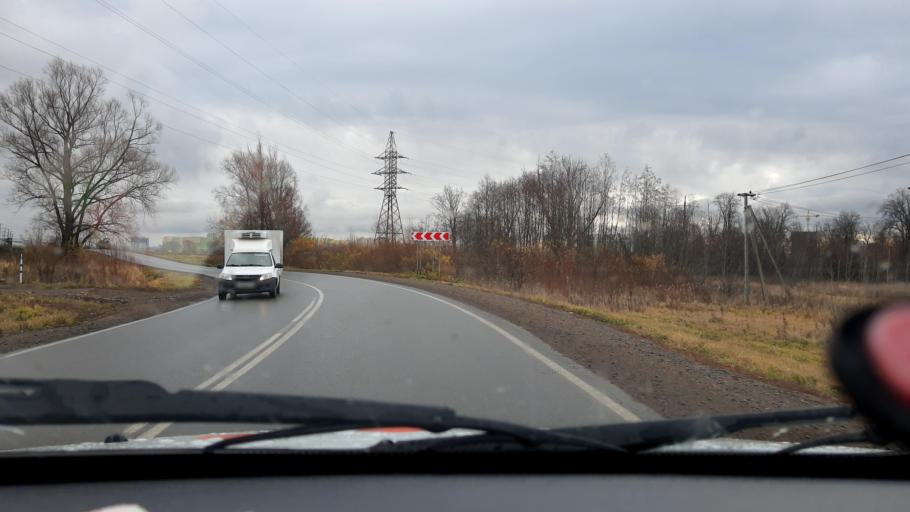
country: RU
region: Bashkortostan
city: Mikhaylovka
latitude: 54.8001
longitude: 55.8370
